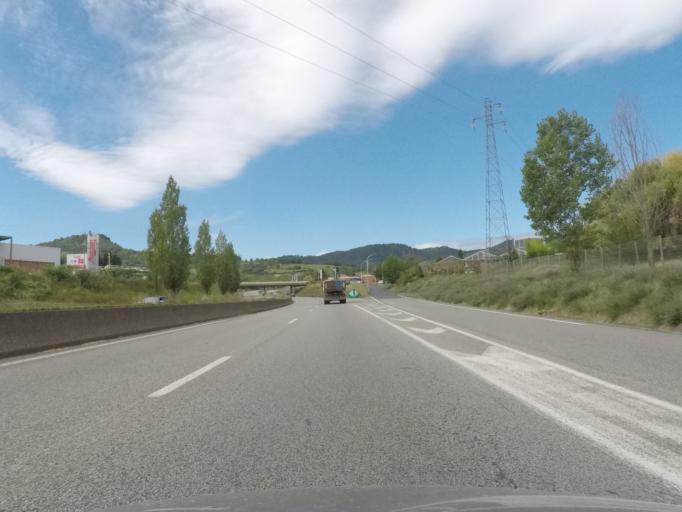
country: FR
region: Auvergne
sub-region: Departement du Puy-de-Dome
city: Beaumont
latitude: 45.7463
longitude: 3.0909
